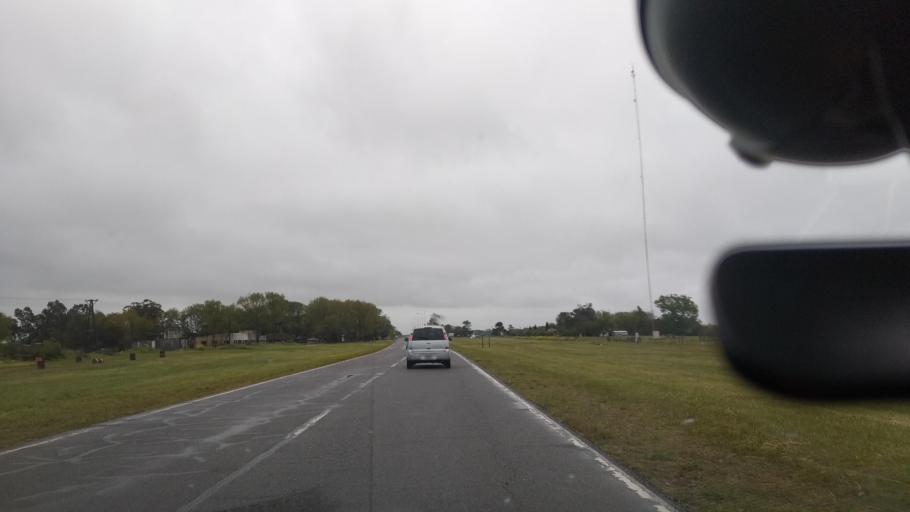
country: AR
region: Buenos Aires
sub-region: Partido de Castelli
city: Castelli
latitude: -35.9798
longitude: -57.4496
